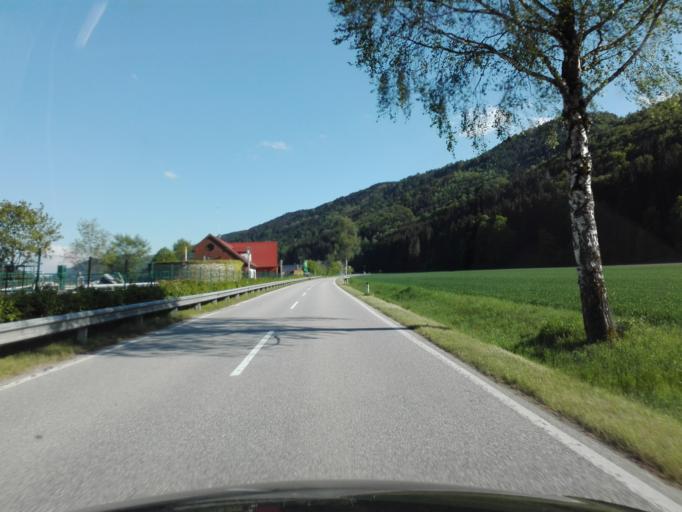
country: AT
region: Upper Austria
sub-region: Politischer Bezirk Rohrbach
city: Pfarrkirchen im Muehlkreis
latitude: 48.4965
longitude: 13.7390
